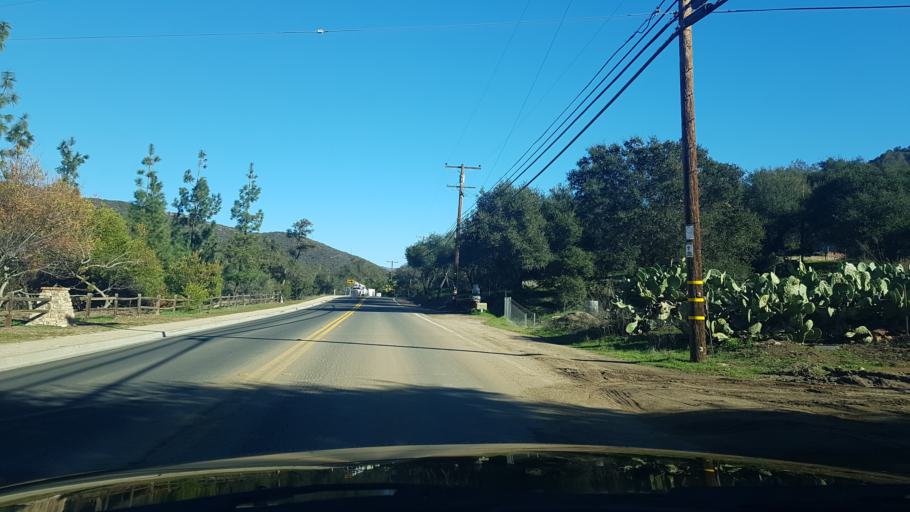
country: US
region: California
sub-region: San Diego County
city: Valley Center
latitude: 33.2052
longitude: -117.0137
